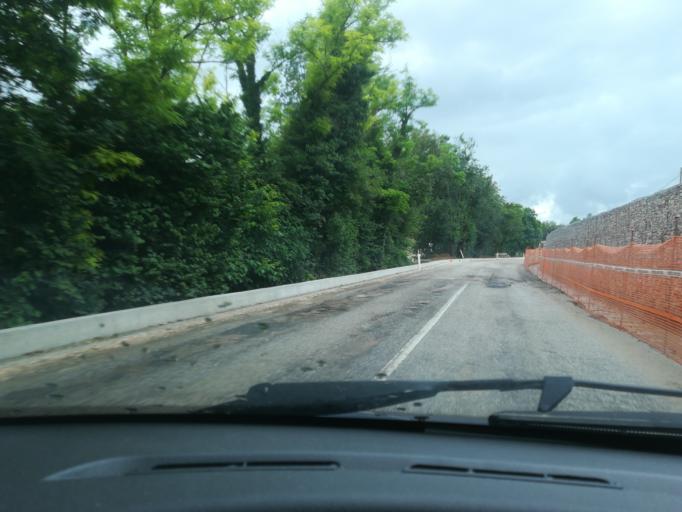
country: IT
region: The Marches
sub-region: Provincia di Macerata
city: San Ginesio
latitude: 43.1013
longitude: 13.3466
